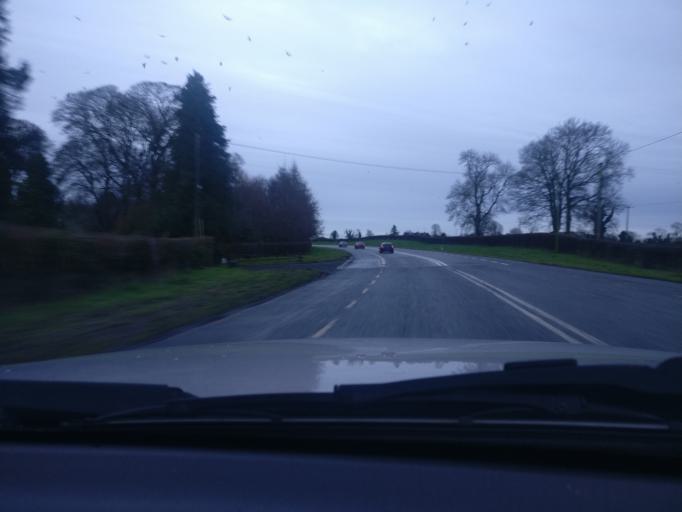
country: IE
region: Leinster
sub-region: An Mhi
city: Kells
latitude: 53.6942
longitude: -6.7871
